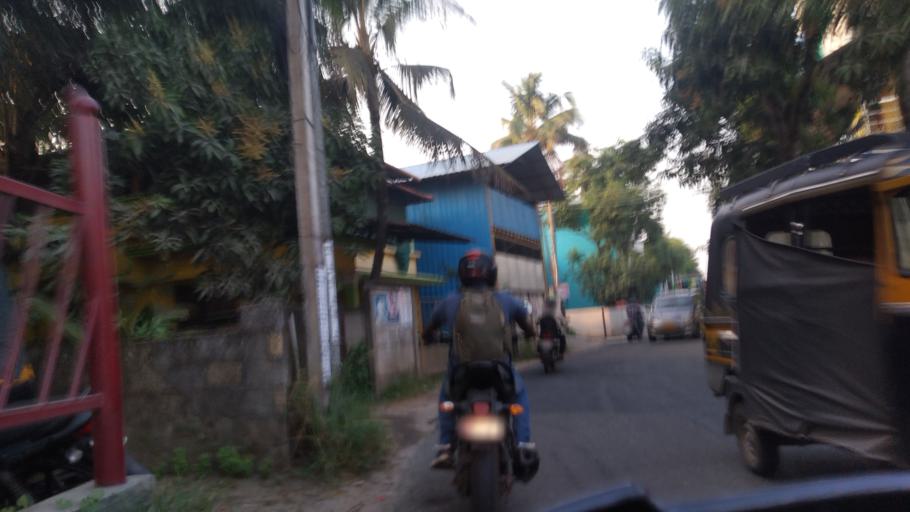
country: IN
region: Kerala
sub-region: Ernakulam
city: Elur
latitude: 10.0347
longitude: 76.2757
